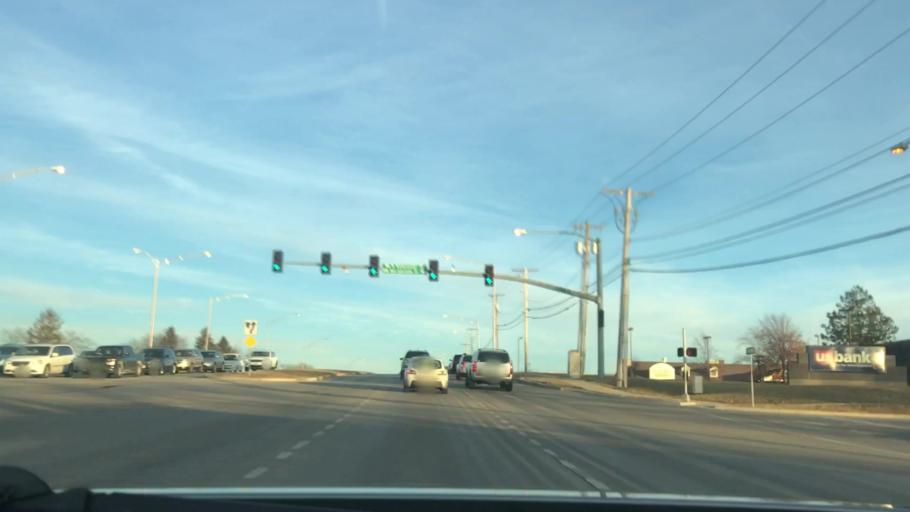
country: US
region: Missouri
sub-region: Platte County
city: Weatherby Lake
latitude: 39.2468
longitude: -94.6517
